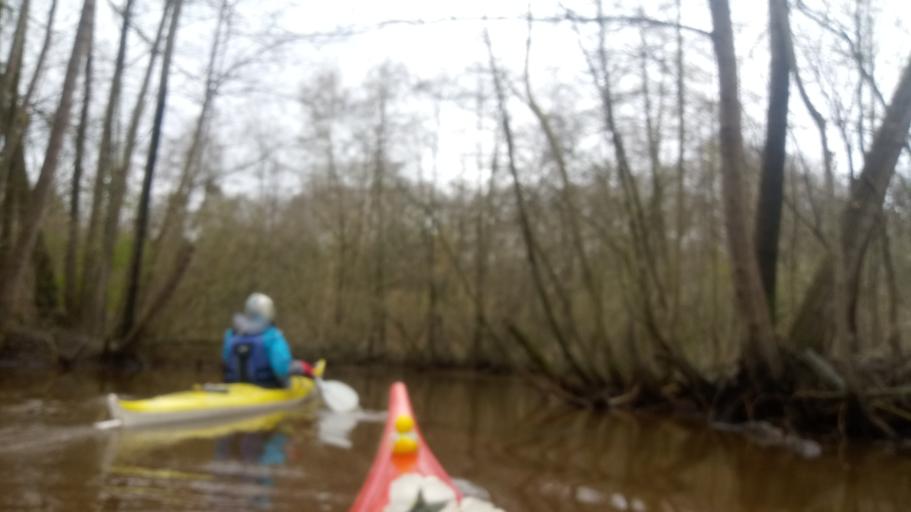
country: NL
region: Groningen
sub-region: Gemeente Vlagtwedde
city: Sellingen
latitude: 52.9492
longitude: 7.1386
